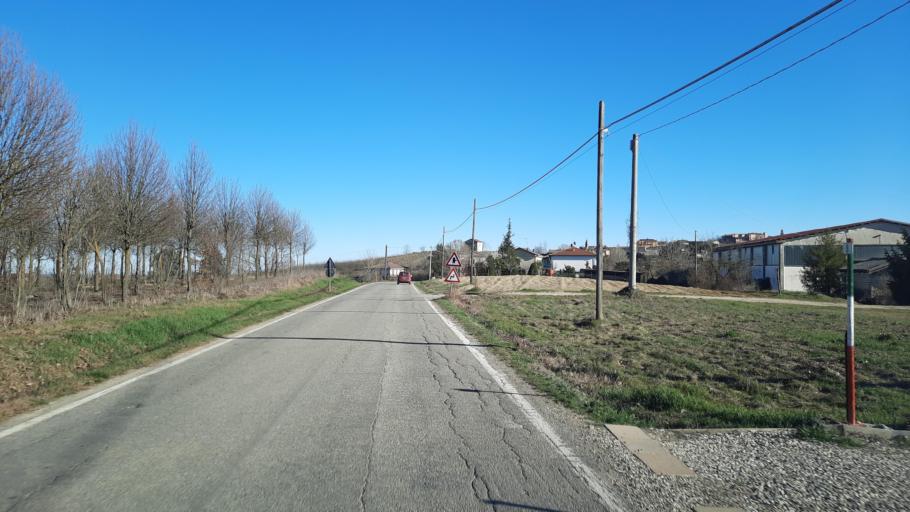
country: IT
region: Piedmont
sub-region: Provincia di Alessandria
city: Frassinello Monferrato
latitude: 45.0393
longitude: 8.3784
